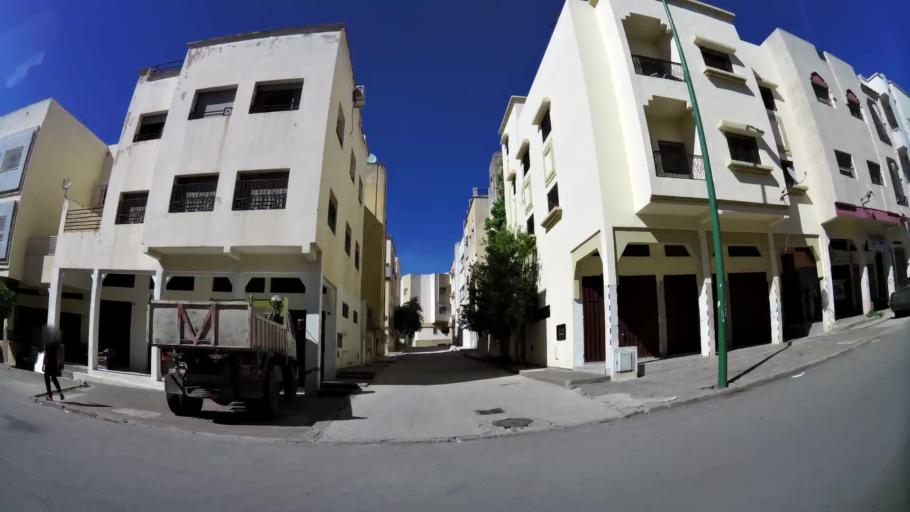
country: MA
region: Fes-Boulemane
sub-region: Fes
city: Fes
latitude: 34.0193
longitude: -4.9841
